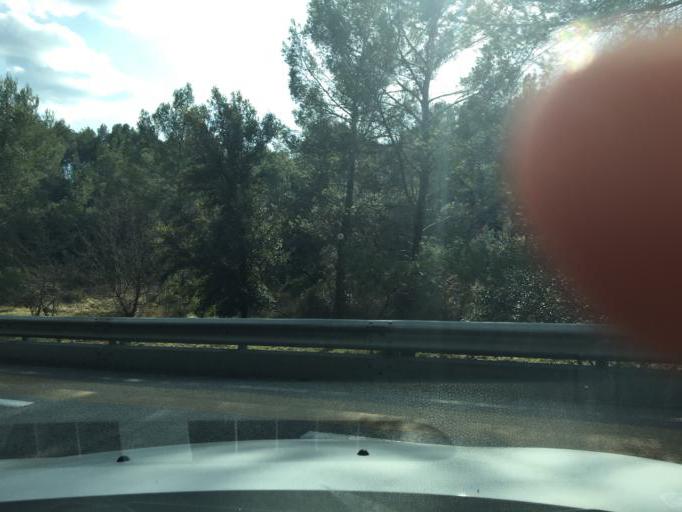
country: FR
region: Provence-Alpes-Cote d'Azur
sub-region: Departement du Var
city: Figanieres
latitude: 43.5753
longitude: 6.4979
